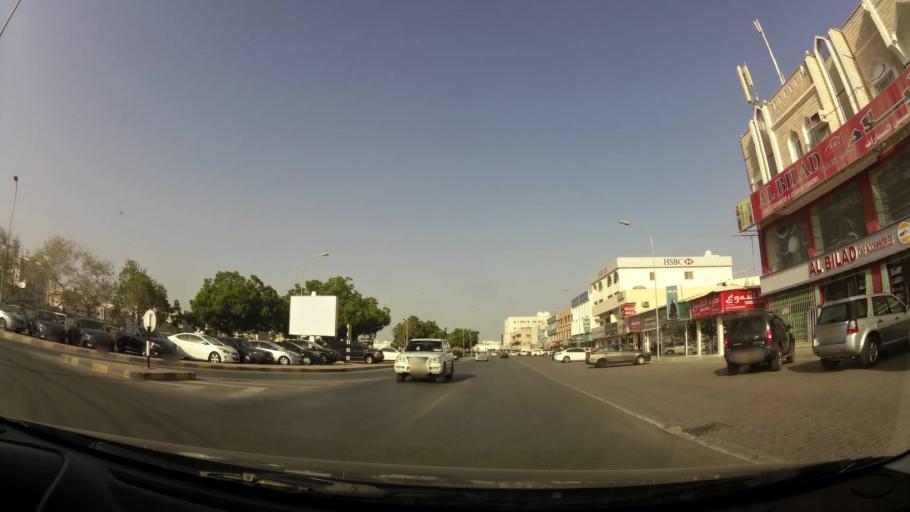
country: OM
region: Zufar
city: Salalah
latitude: 17.0110
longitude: 54.0860
